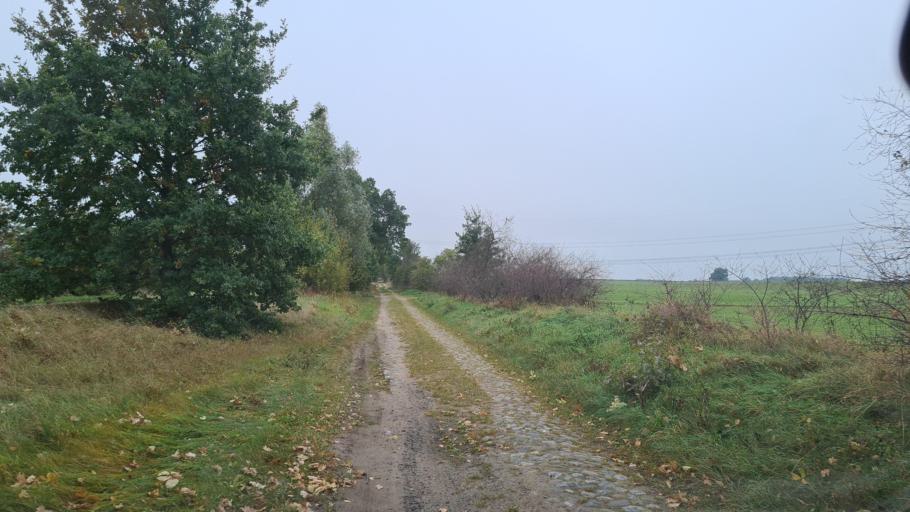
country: DE
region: Brandenburg
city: Furstenwalde
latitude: 52.4240
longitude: 14.0238
